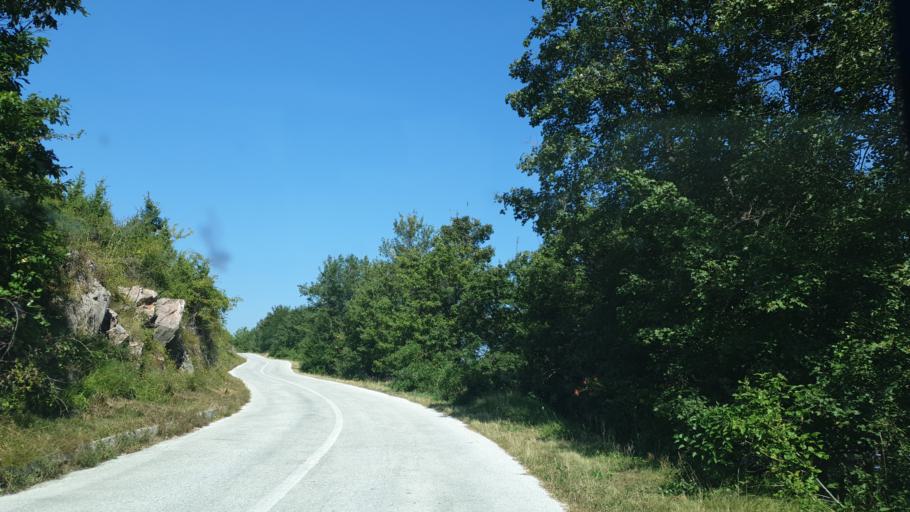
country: RS
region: Central Serbia
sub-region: Zlatiborski Okrug
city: Cajetina
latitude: 43.6805
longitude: 19.8460
